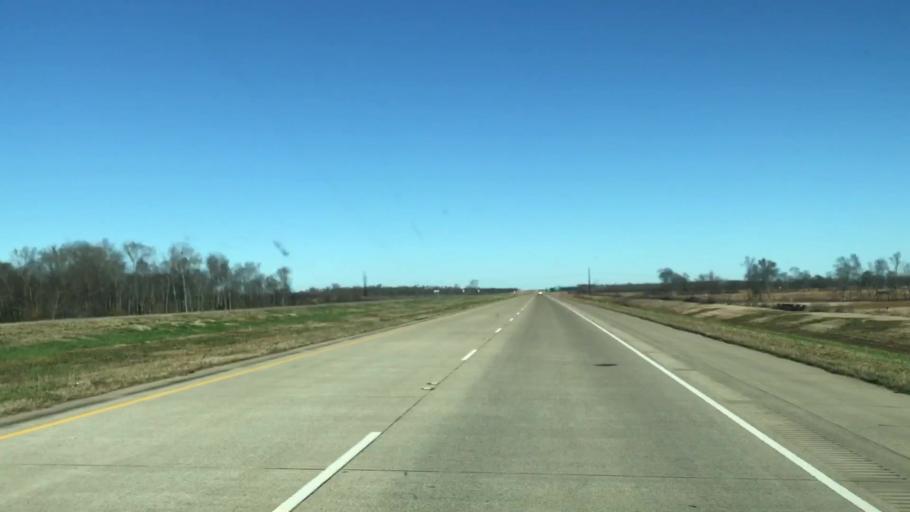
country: US
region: Louisiana
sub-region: Caddo Parish
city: Blanchard
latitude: 32.6585
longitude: -93.8433
